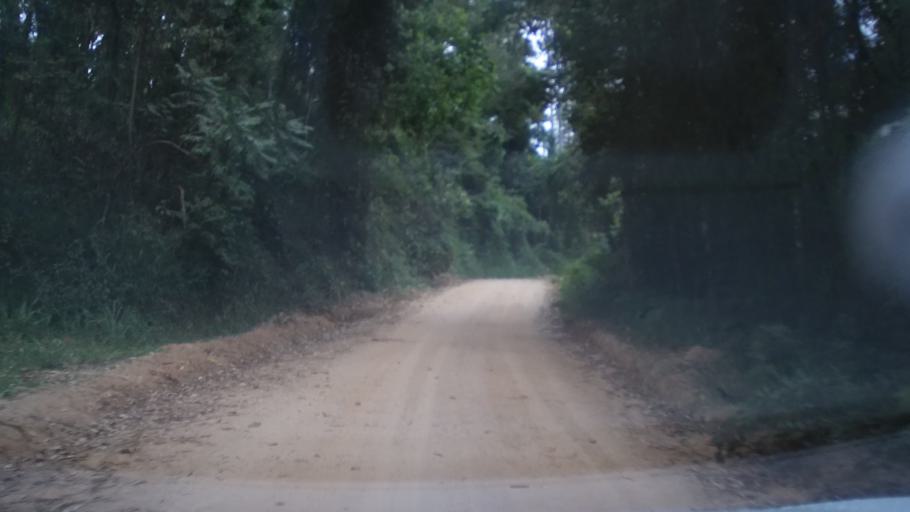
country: BR
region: Sao Paulo
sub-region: Itupeva
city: Itupeva
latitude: -23.1883
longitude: -47.0608
